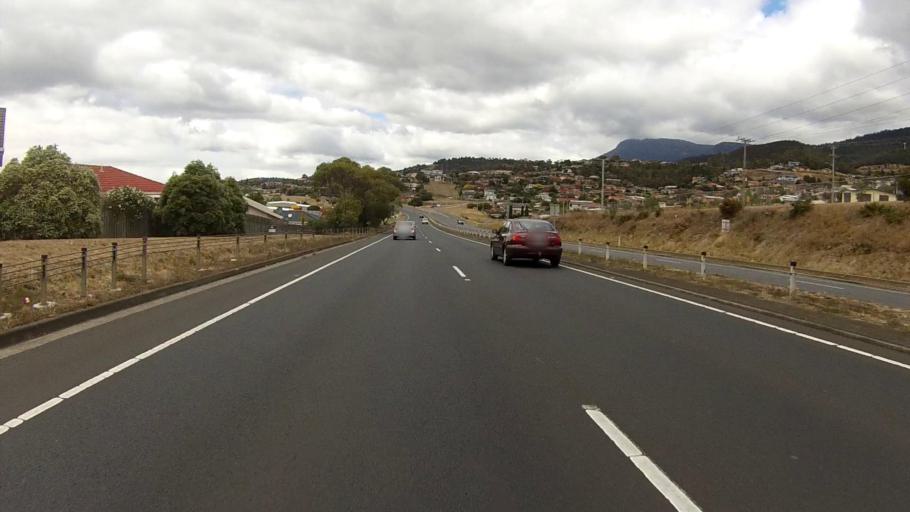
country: AU
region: Tasmania
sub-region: Glenorchy
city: Berriedale
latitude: -42.8115
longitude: 147.2505
